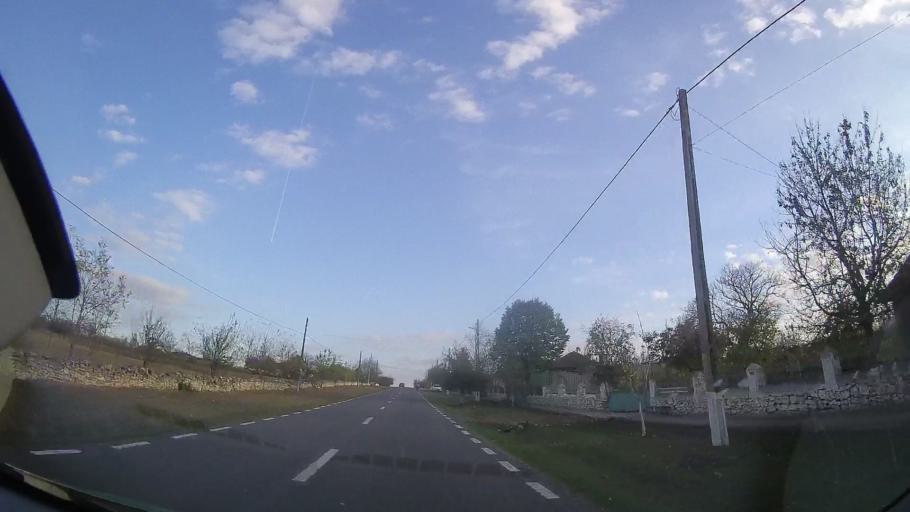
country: RO
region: Constanta
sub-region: Comuna Chirnogeni
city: Plopeni
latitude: 43.9601
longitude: 28.1443
